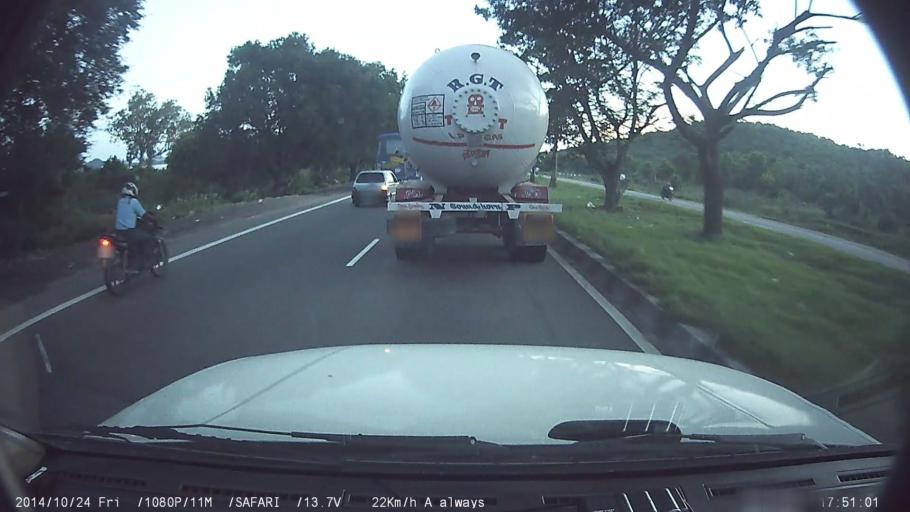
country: IN
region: Tamil Nadu
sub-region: Kancheepuram
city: Chengalpattu
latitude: 12.7201
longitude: 79.9812
